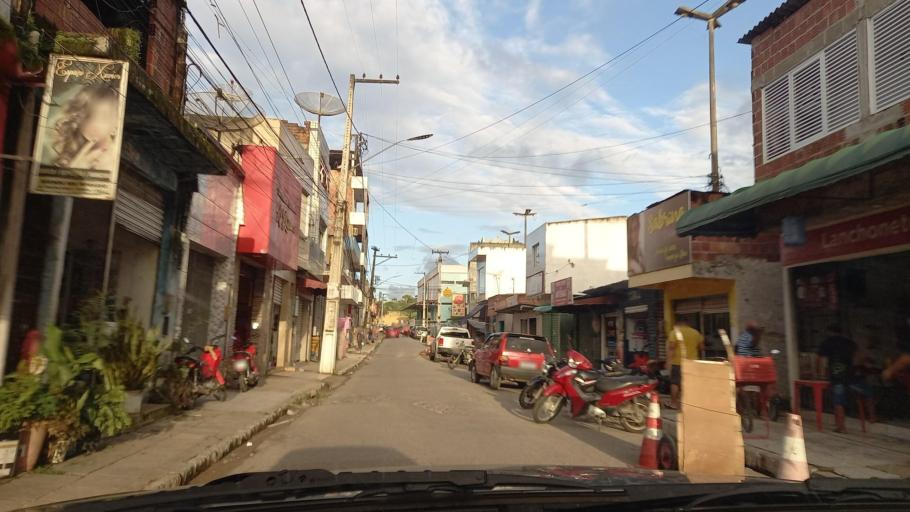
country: BR
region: Pernambuco
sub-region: Palmares
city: Palmares
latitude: -8.6862
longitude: -35.5939
